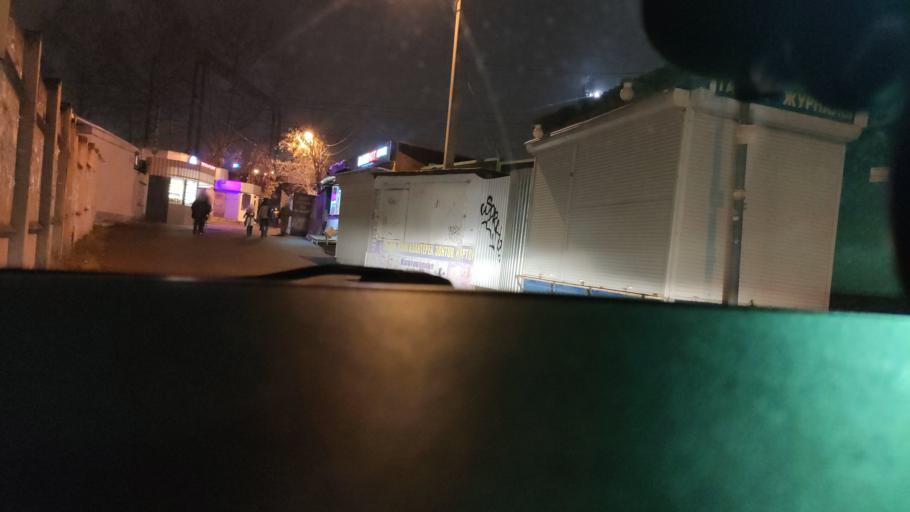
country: RU
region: Perm
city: Perm
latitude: 58.0058
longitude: 56.1843
